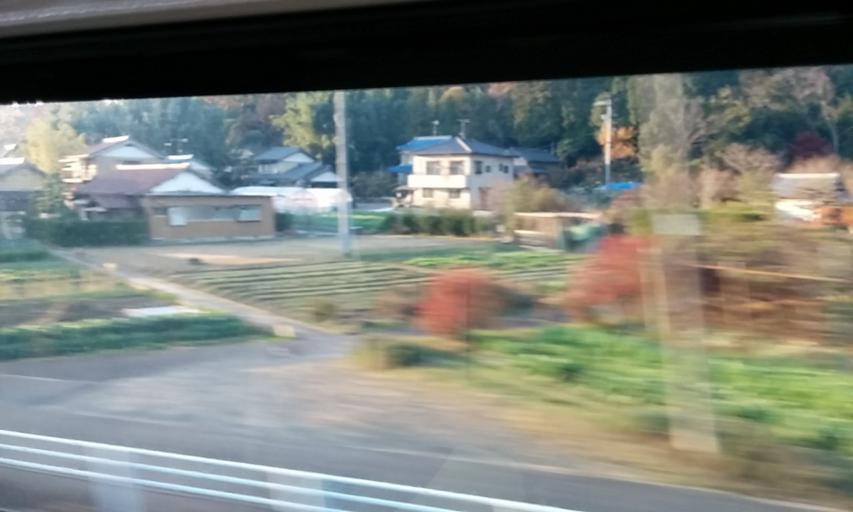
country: JP
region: Aichi
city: Seto
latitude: 35.2689
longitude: 137.0722
